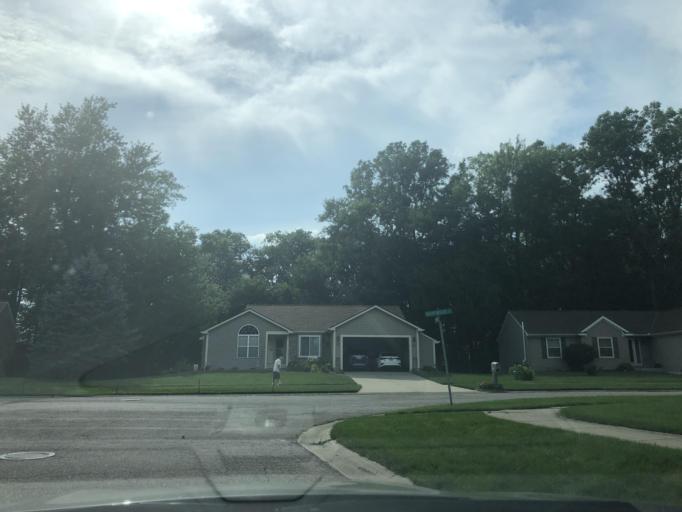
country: US
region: Michigan
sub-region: Ingham County
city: Holt
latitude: 42.6490
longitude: -84.4970
